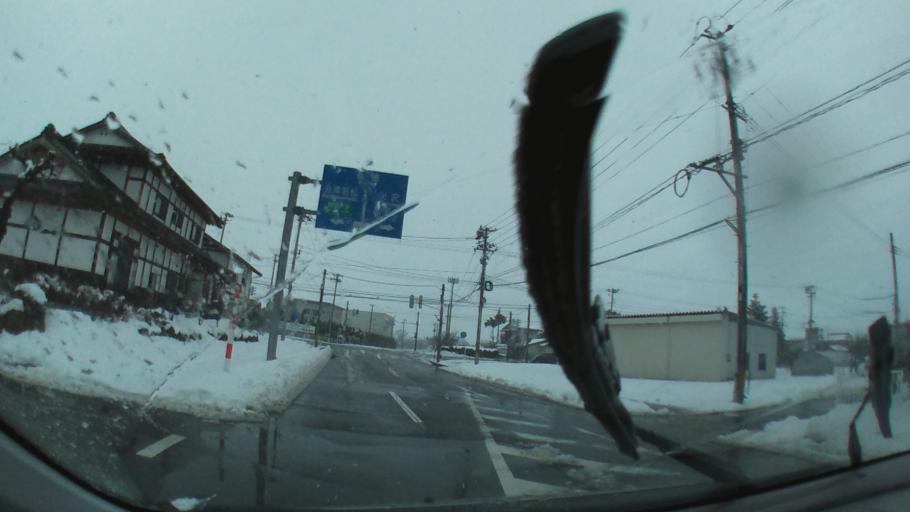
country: JP
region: Fukushima
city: Kitakata
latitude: 37.6038
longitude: 139.8937
